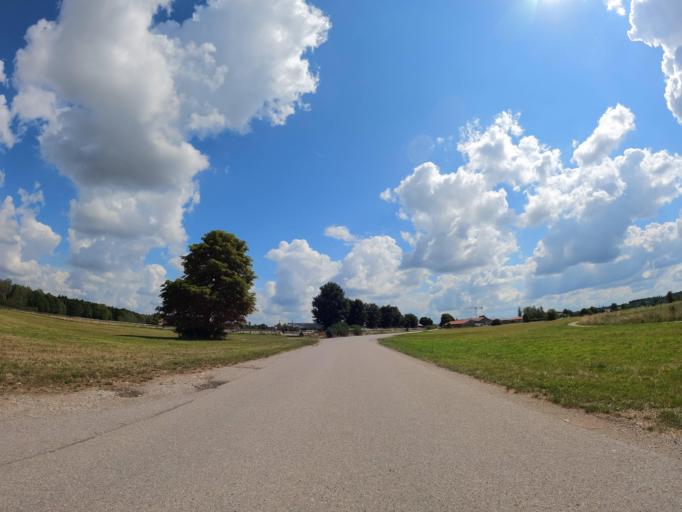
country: DE
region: Bavaria
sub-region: Upper Bavaria
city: Brunnthal
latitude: 48.0313
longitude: 11.6719
